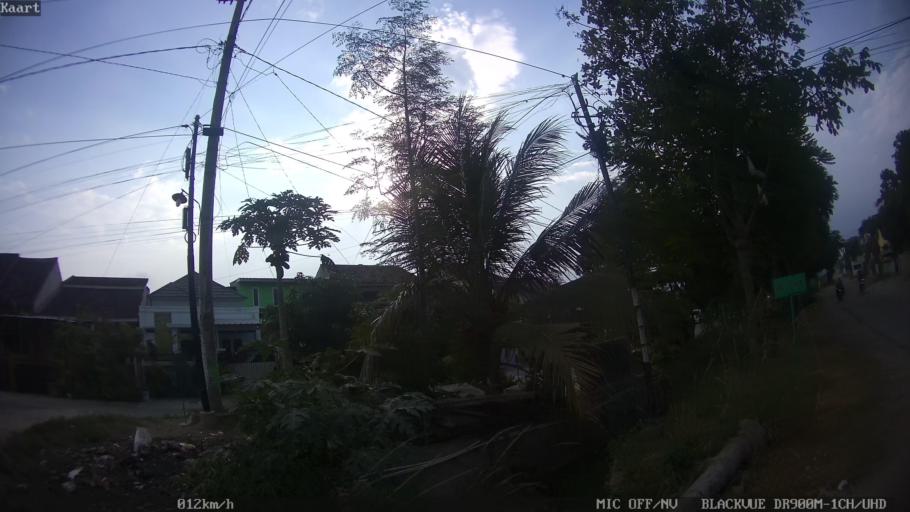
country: ID
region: Lampung
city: Kedaton
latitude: -5.4052
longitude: 105.3051
